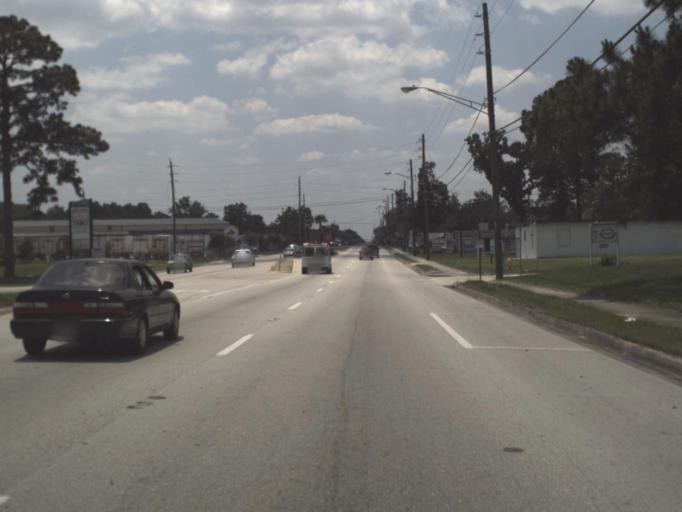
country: US
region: Florida
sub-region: Duval County
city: Jacksonville
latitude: 30.3593
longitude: -81.7313
